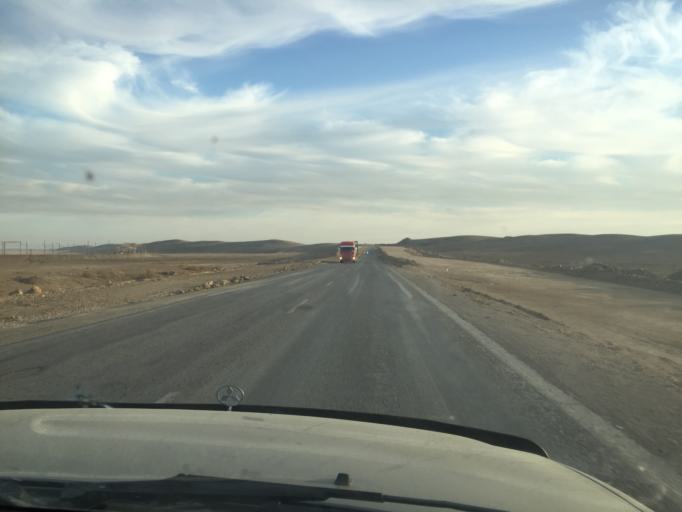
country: KZ
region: Almaty Oblysy
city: Ulken
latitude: 45.0884
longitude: 73.9674
